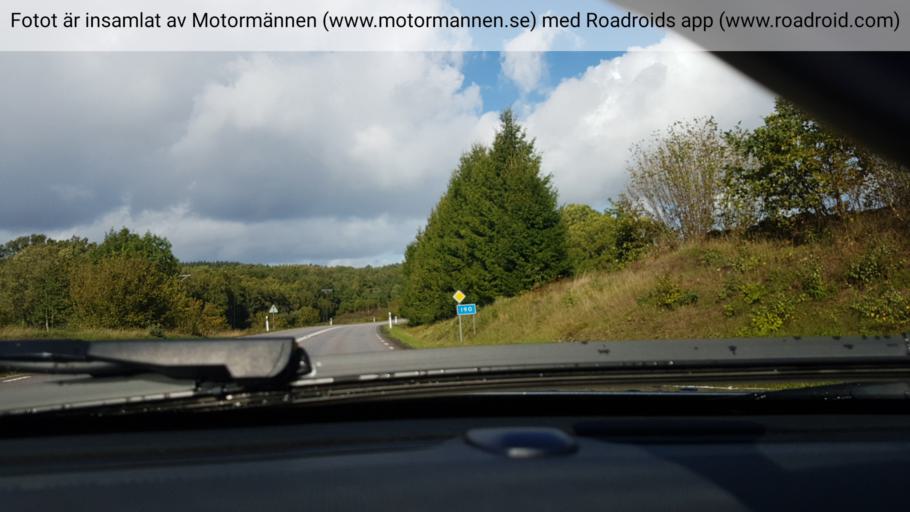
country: SE
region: Vaestra Goetaland
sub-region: Alingsas Kommun
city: Sollebrunn
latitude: 58.0562
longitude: 12.4655
